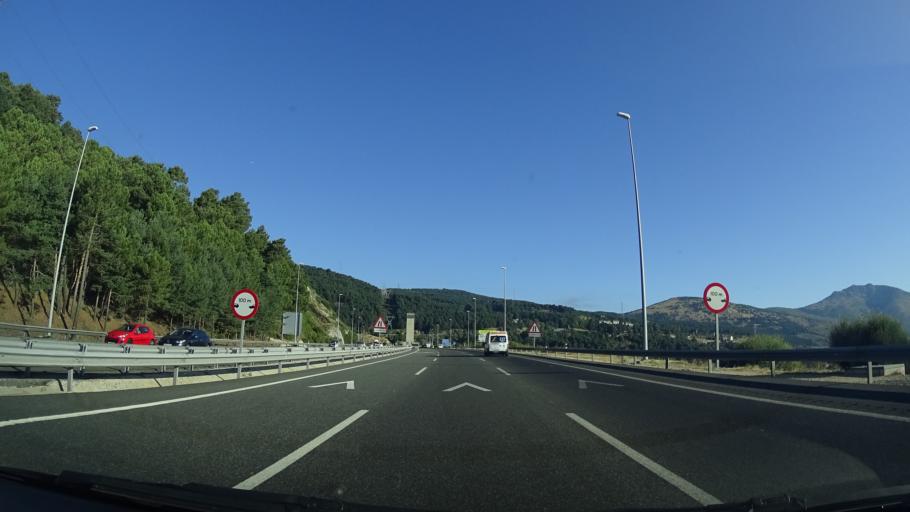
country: ES
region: Madrid
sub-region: Provincia de Madrid
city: Guadarrama
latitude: 40.6943
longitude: -4.1247
